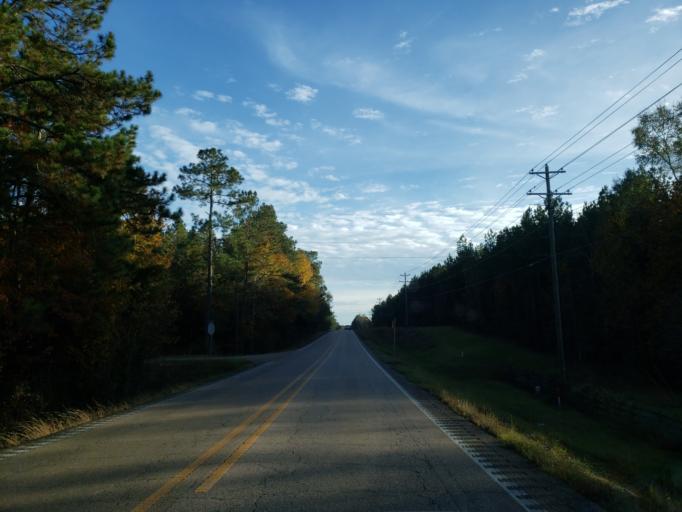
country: US
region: Mississippi
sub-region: Lamar County
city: West Hattiesburg
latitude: 31.3071
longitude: -89.4708
